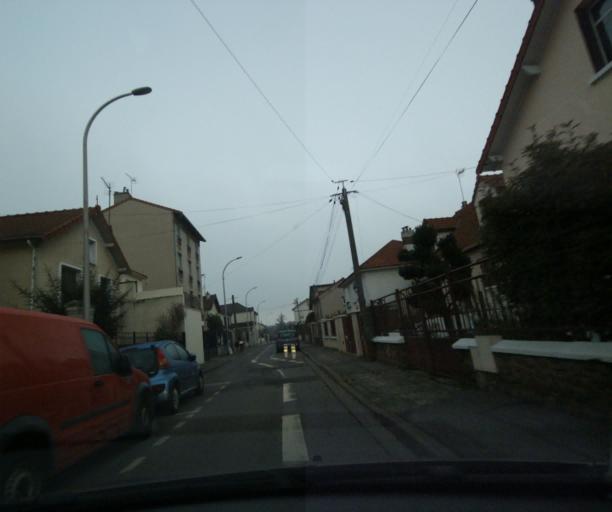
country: FR
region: Ile-de-France
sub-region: Departement du Val-de-Marne
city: Le Perreux-sur-Marne
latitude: 48.8529
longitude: 2.5015
